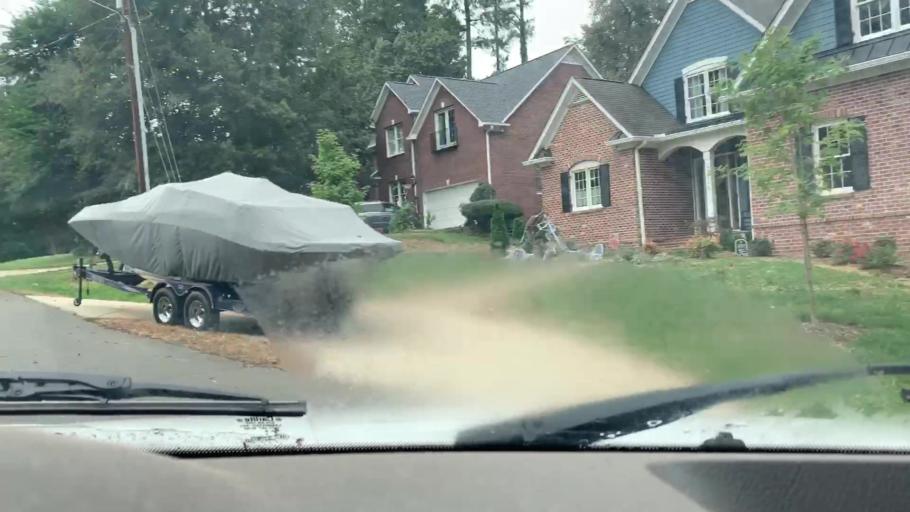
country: US
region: North Carolina
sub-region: Mecklenburg County
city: Cornelius
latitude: 35.4960
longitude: -80.9119
